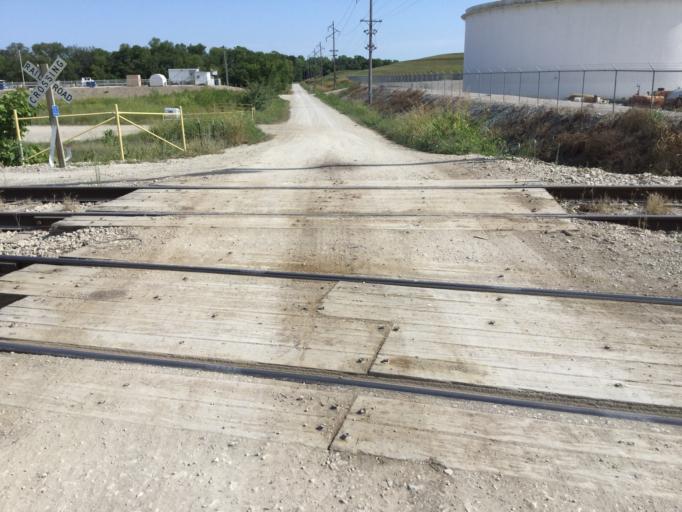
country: US
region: Kansas
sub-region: Montgomery County
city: Coffeyville
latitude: 37.0509
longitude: -95.6111
